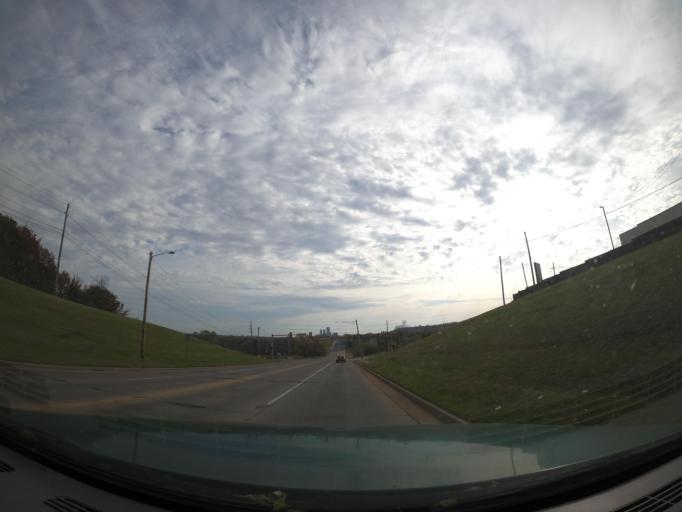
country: US
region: Oklahoma
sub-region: Tulsa County
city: Turley
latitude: 36.2067
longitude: -95.9936
